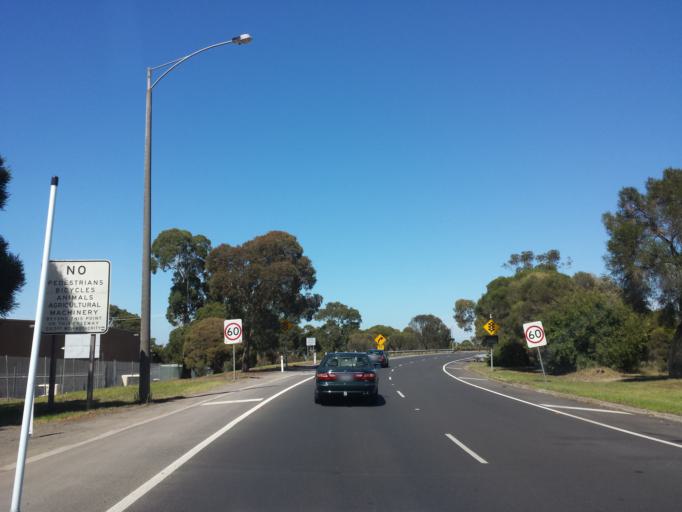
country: AU
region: Victoria
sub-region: Monash
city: Notting Hill
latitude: -37.9039
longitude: 145.1570
